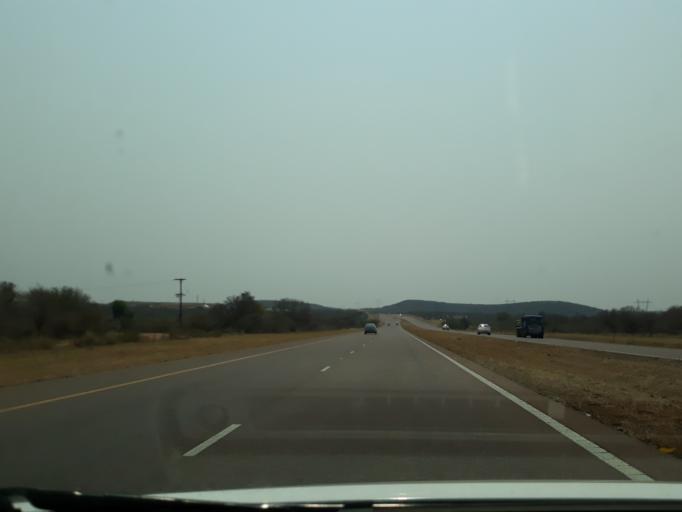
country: BW
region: Kgatleng
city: Bokaa
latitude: -24.4081
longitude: 26.0529
